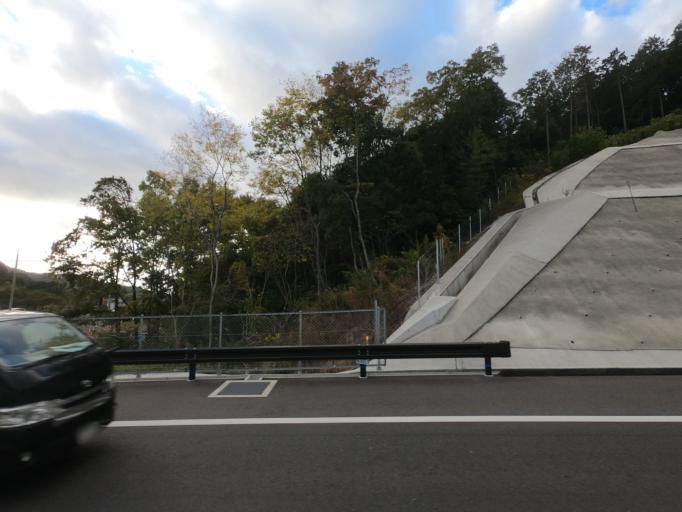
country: JP
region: Kumamoto
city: Minamata
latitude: 32.2102
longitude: 130.4203
